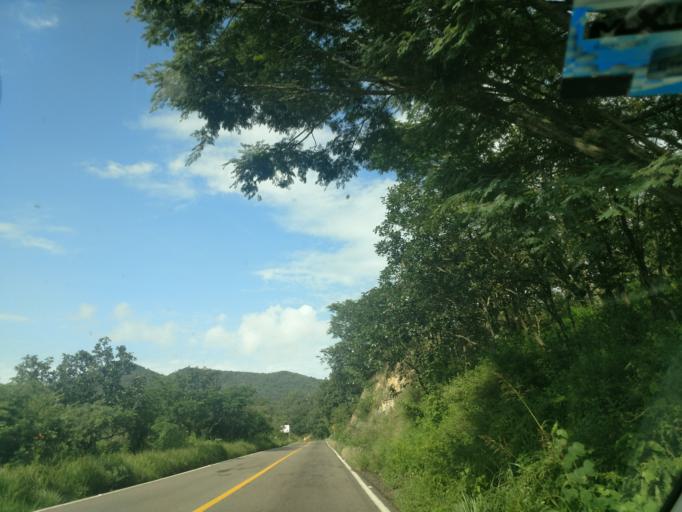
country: MX
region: Jalisco
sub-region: Atengo
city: Soyatlan del Oro
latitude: 20.4968
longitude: -104.3569
